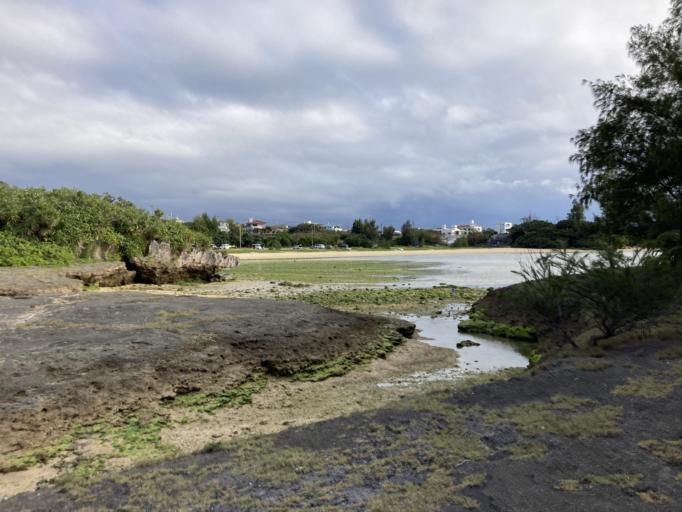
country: JP
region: Okinawa
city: Itoman
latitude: 26.1088
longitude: 127.6601
